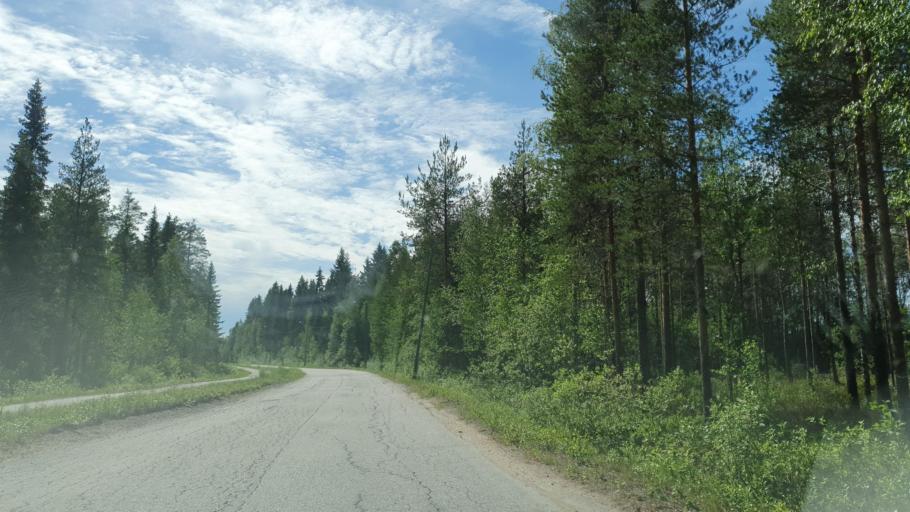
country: FI
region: Kainuu
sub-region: Kehys-Kainuu
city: Hyrynsalmi
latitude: 64.6868
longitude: 28.4673
